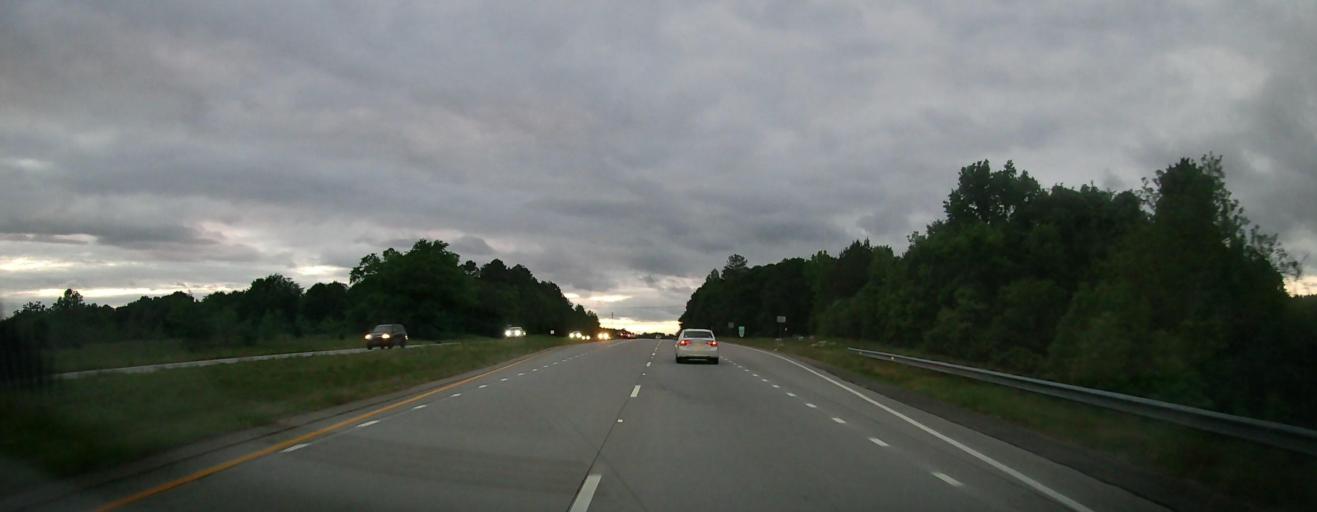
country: US
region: Georgia
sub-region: Jackson County
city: Arcade
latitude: 34.0902
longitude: -83.5830
